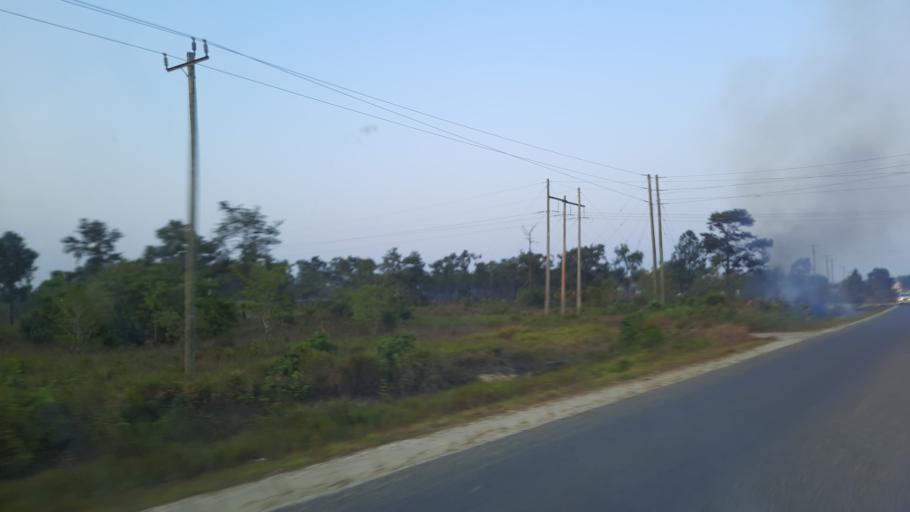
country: BZ
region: Stann Creek
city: Placencia
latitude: 16.5348
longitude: -88.4291
